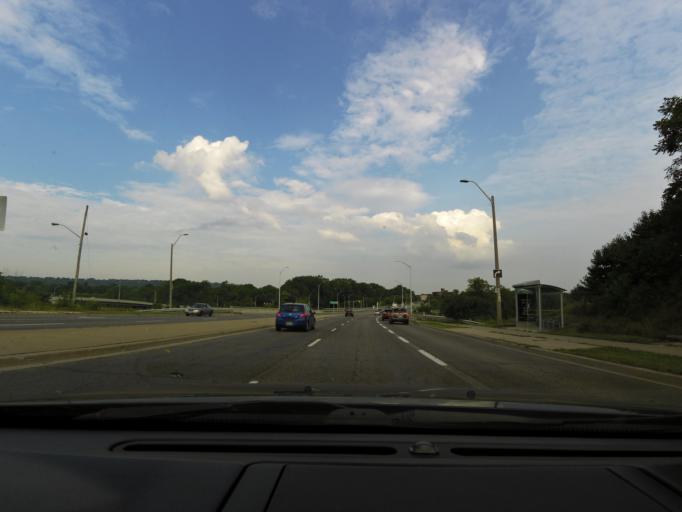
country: CA
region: Ontario
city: Hamilton
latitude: 43.2258
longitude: -79.7889
